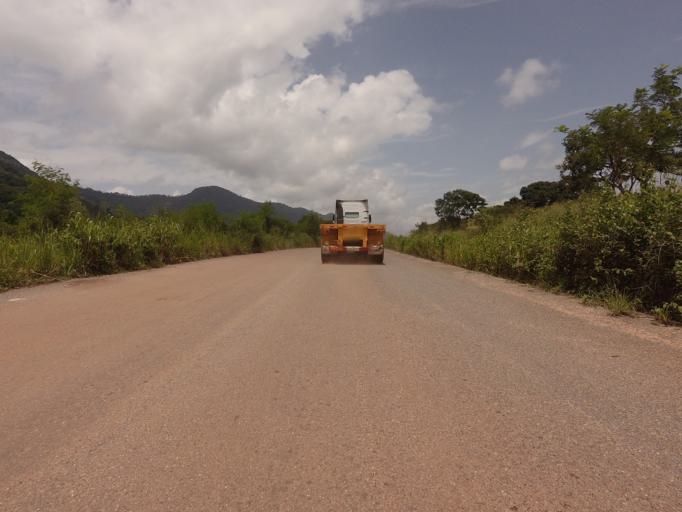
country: GH
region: Volta
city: Ho
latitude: 6.7799
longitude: 0.3654
